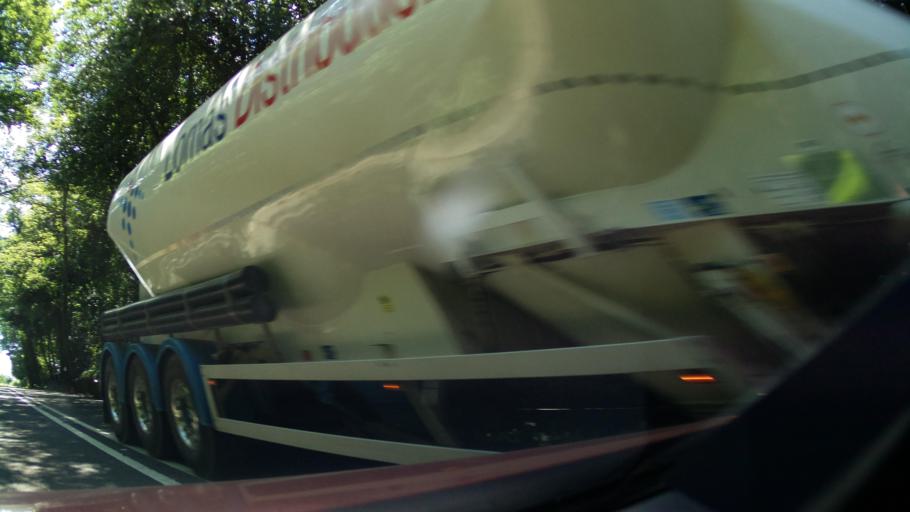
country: GB
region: England
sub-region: Derbyshire
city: Ashbourne
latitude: 53.0444
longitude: -1.7377
